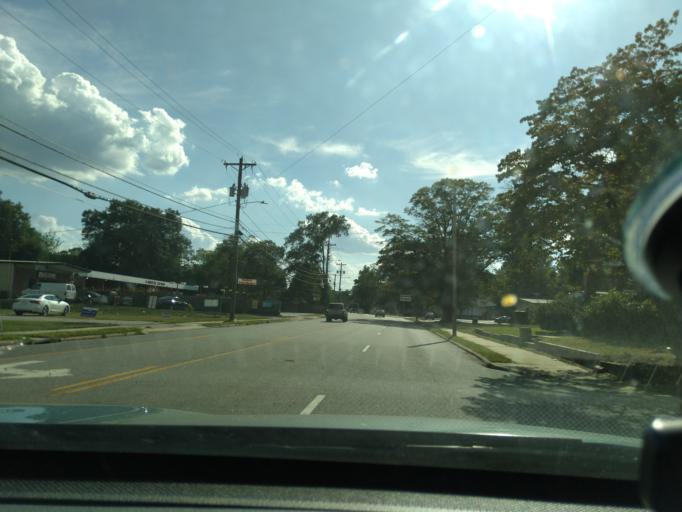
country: US
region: North Carolina
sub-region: Nash County
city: Rocky Mount
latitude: 35.9306
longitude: -77.8136
